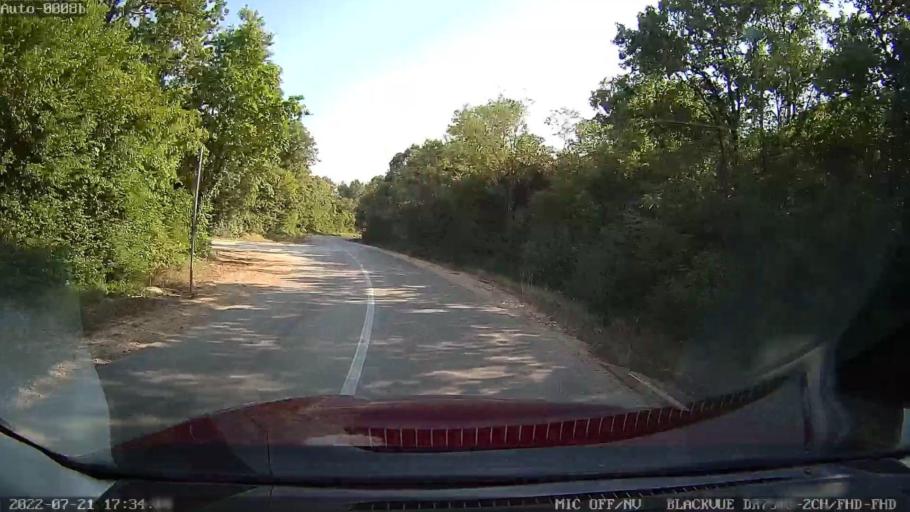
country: HR
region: Istarska
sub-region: Grad Rovinj
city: Rovinj
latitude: 45.1675
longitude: 13.7446
